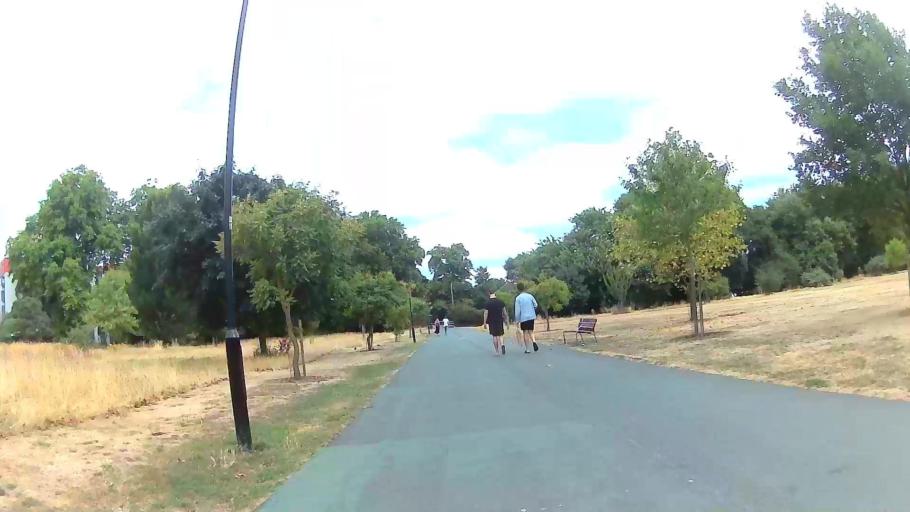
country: GB
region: England
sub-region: Greater London
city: Hackney
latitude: 51.5600
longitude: -0.0448
